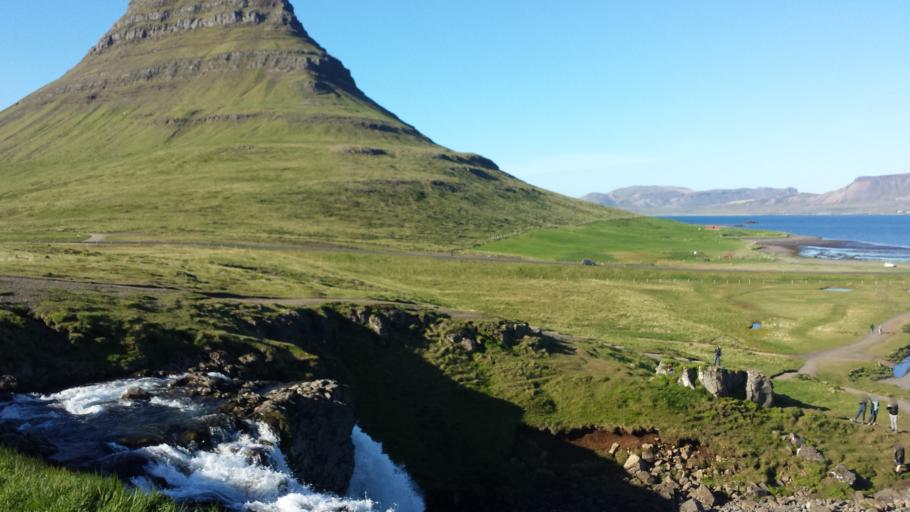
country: IS
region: West
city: Olafsvik
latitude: 64.9261
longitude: -23.3125
